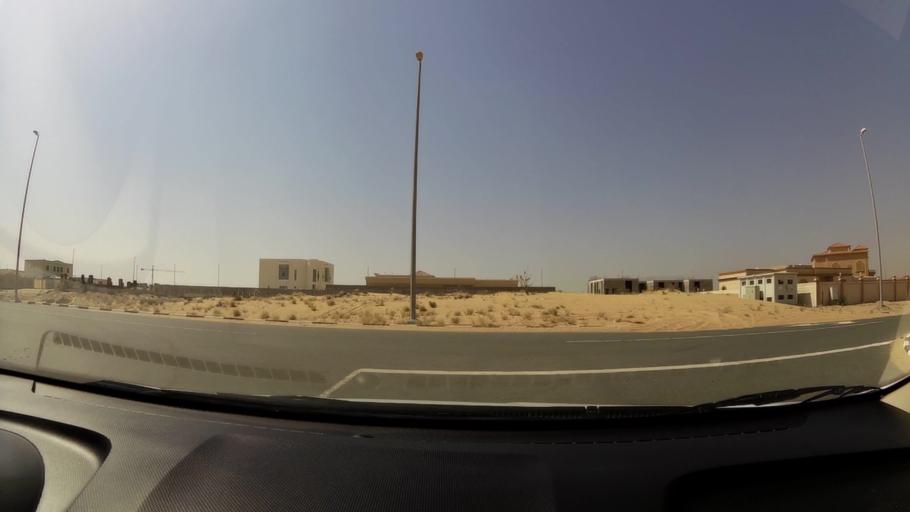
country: AE
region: Umm al Qaywayn
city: Umm al Qaywayn
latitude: 25.4922
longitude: 55.6098
